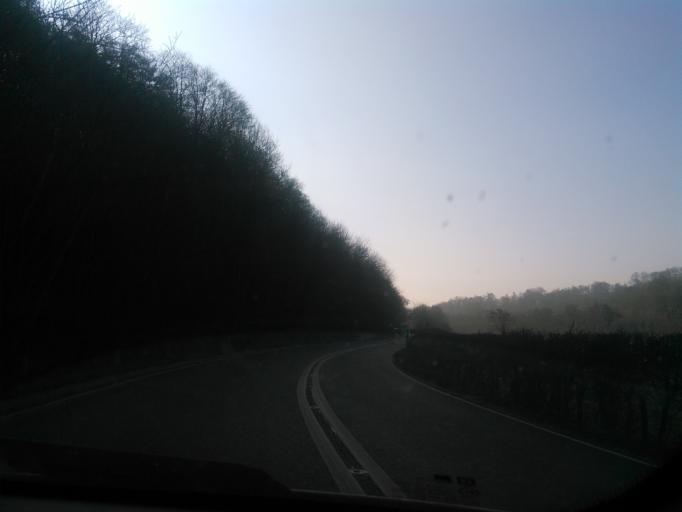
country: GB
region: England
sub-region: Shropshire
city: Church Stretton
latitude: 52.5024
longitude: -2.8200
